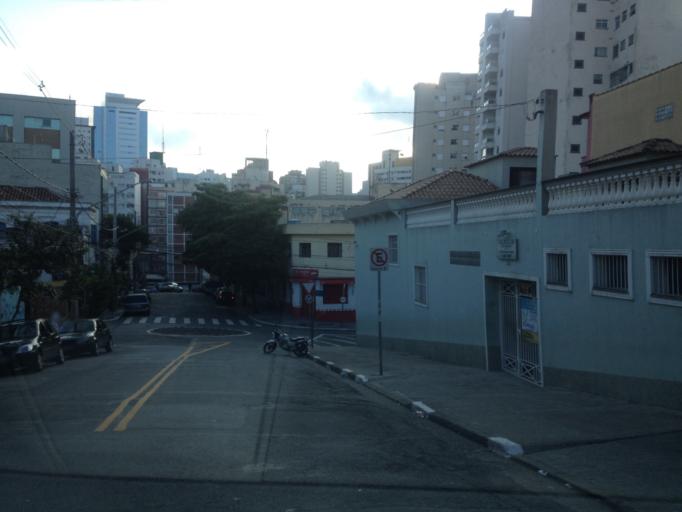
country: BR
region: Sao Paulo
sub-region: Sao Paulo
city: Sao Paulo
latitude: -23.5565
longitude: -46.6474
